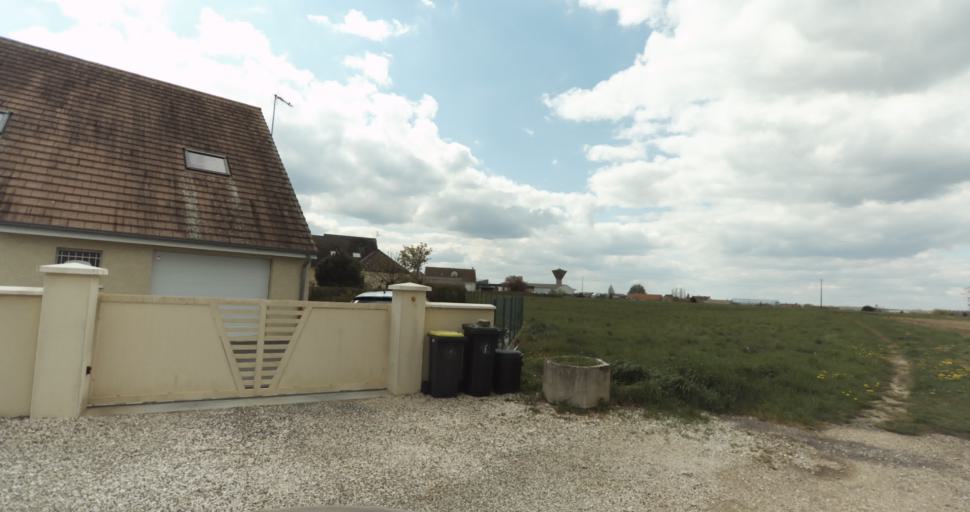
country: FR
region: Bourgogne
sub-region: Departement de la Cote-d'Or
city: Auxonne
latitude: 47.1815
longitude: 5.4066
